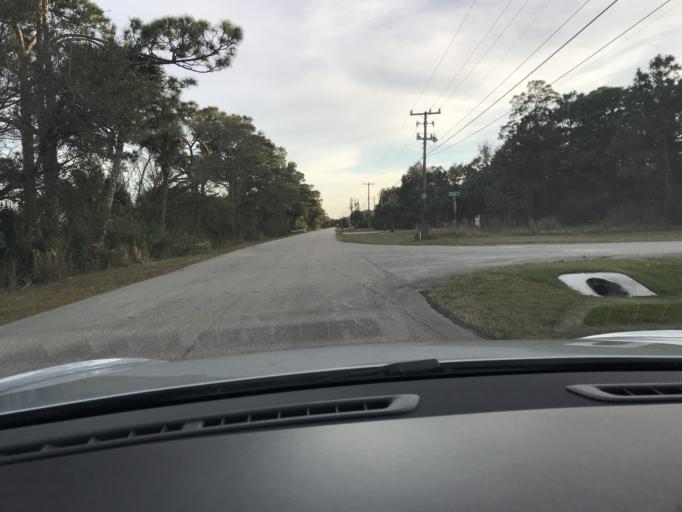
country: US
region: Florida
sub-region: Saint Lucie County
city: Lakewood Park
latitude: 27.4911
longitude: -80.3741
